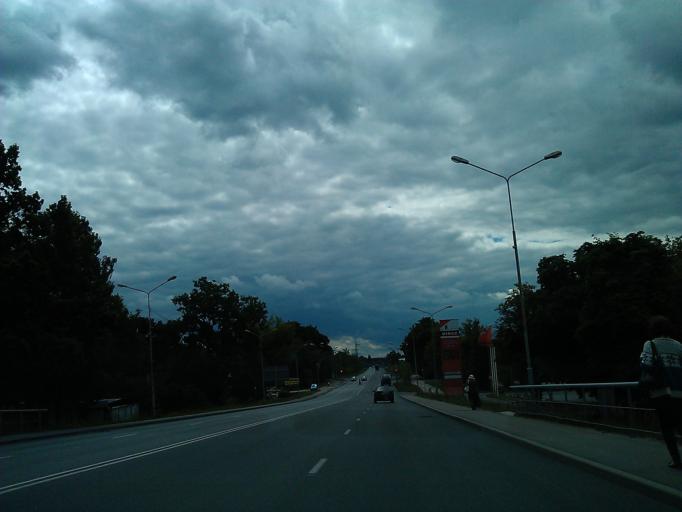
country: LV
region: Jelgava
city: Jelgava
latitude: 56.6372
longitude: 23.7286
